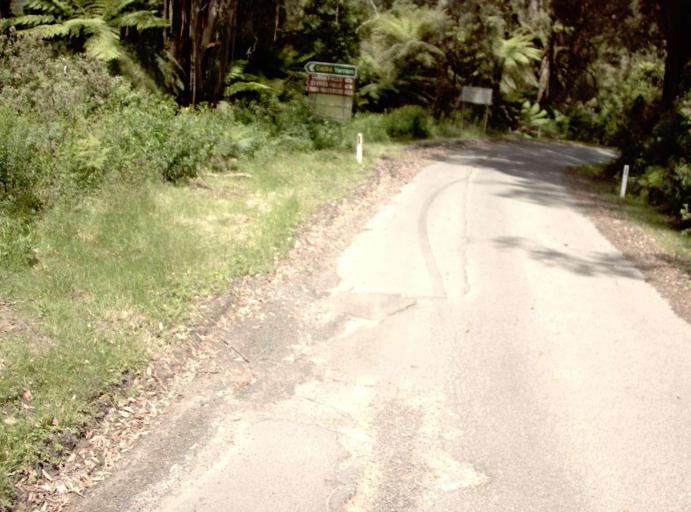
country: AU
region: Victoria
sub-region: Latrobe
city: Morwell
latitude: -38.4368
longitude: 146.5275
